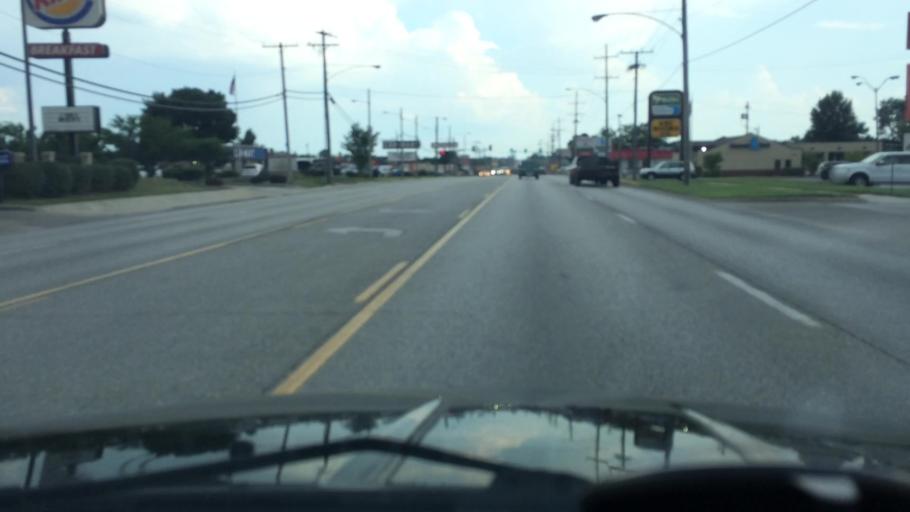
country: US
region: Missouri
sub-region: Greene County
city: Springfield
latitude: 37.2362
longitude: -93.2611
